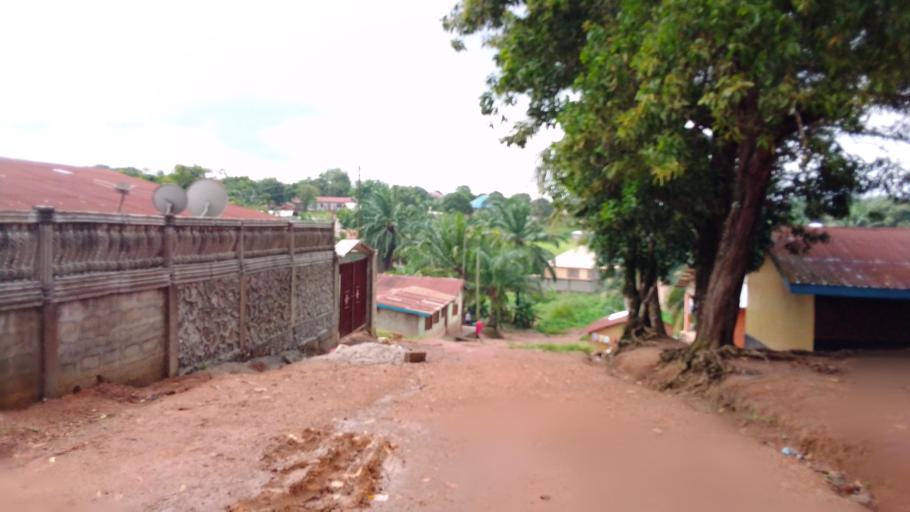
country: SL
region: Eastern Province
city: Kenema
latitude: 7.8723
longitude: -11.1761
